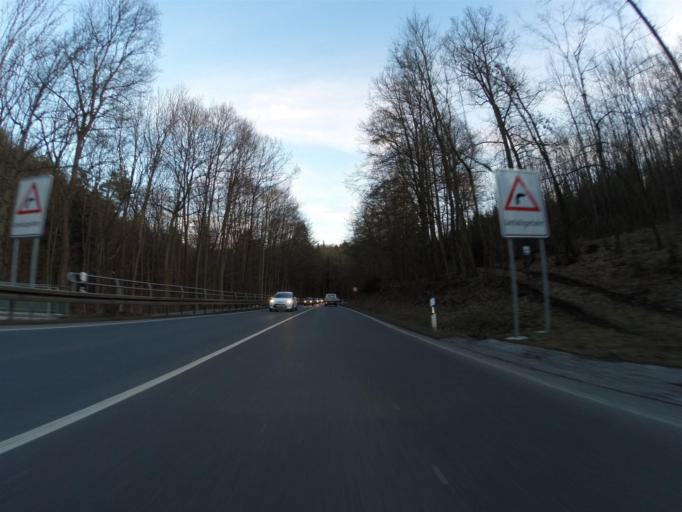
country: DE
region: Thuringia
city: Lehesten
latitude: 50.9535
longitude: 11.5365
